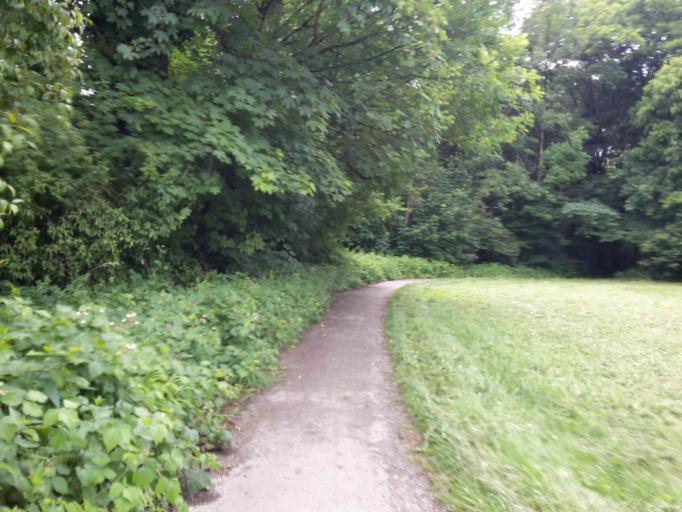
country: DE
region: Bavaria
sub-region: Upper Bavaria
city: Karlsfeld
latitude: 48.1859
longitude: 11.4854
